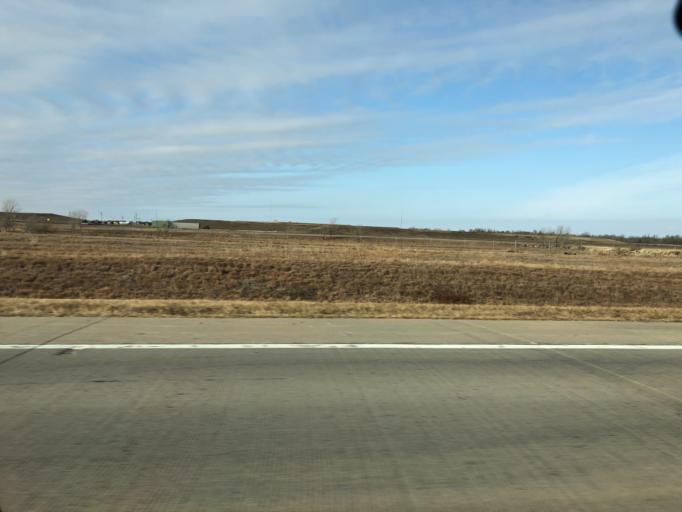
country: US
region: Kansas
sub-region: Reno County
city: South Hutchinson
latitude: 38.0432
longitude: -97.9857
